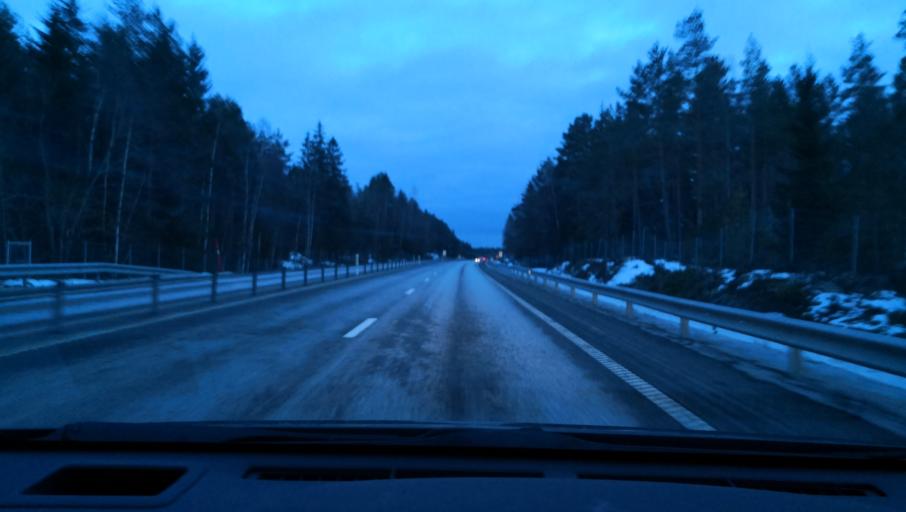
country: SE
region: Vaestmanland
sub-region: Surahammars Kommun
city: Surahammar
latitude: 59.7070
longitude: 16.2464
